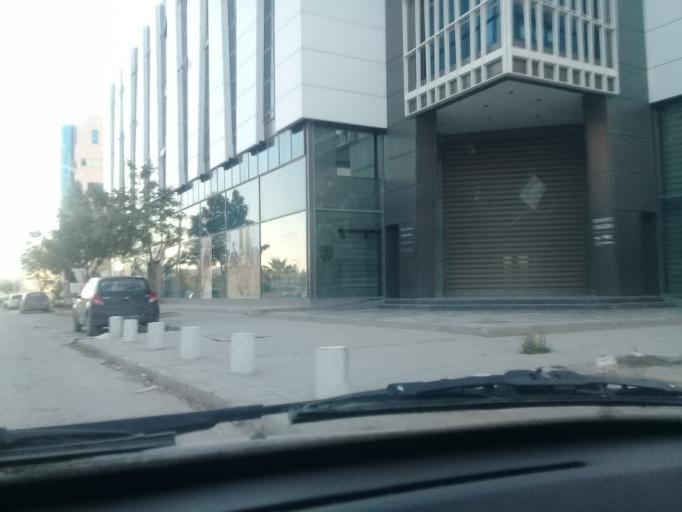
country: TN
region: Tunis
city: La Goulette
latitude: 36.8442
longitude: 10.2704
